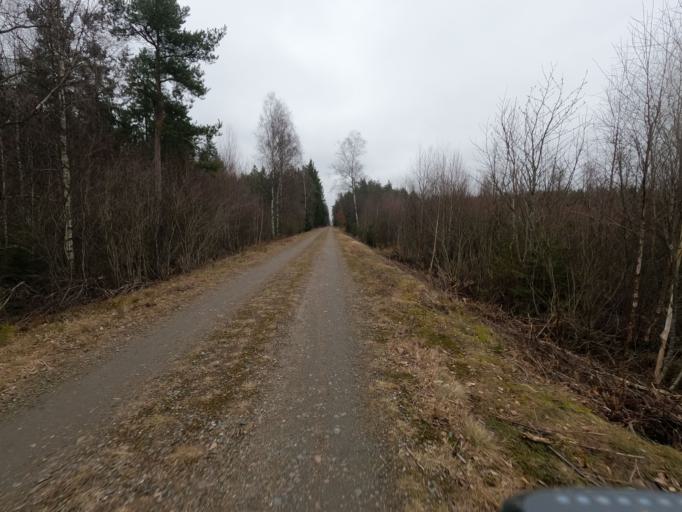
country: SE
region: Kronoberg
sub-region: Ljungby Kommun
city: Ljungby
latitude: 56.8262
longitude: 13.8891
